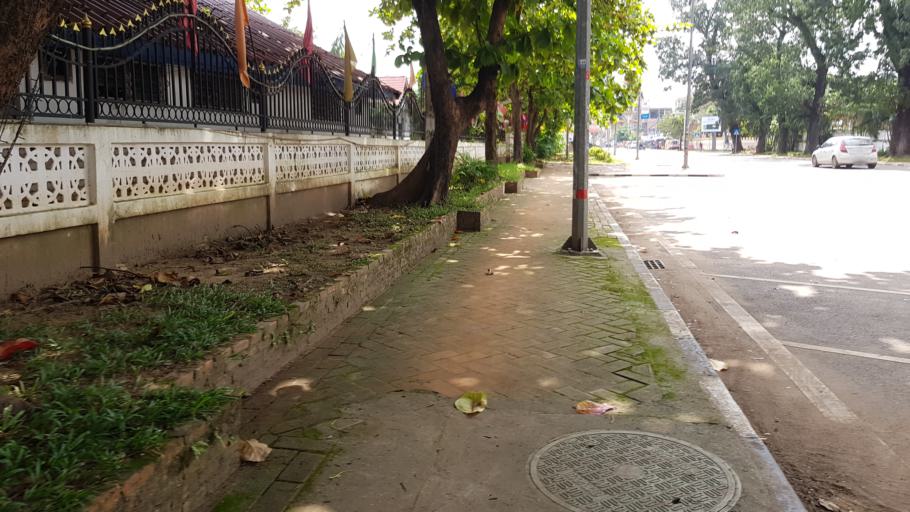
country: LA
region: Vientiane
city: Vientiane
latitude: 17.9604
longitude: 102.6138
